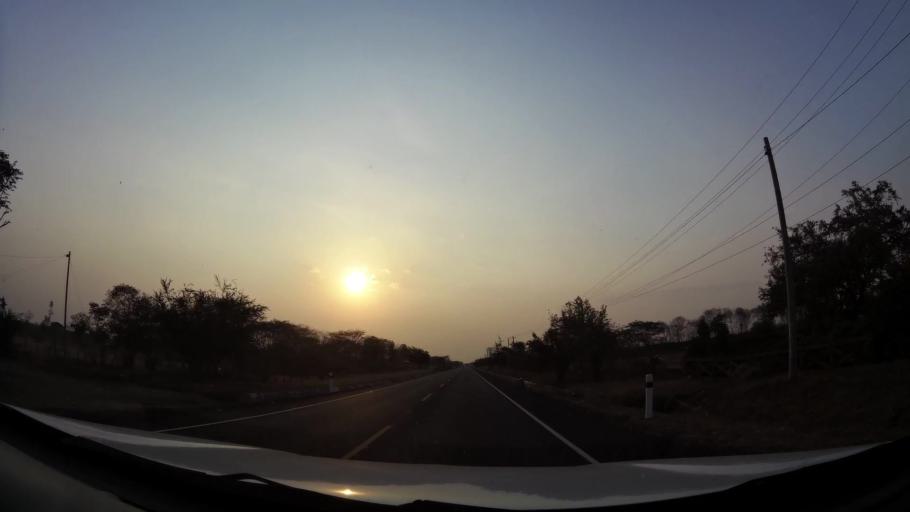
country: NI
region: Leon
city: La Paz Centro
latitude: 12.3202
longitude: -86.6160
